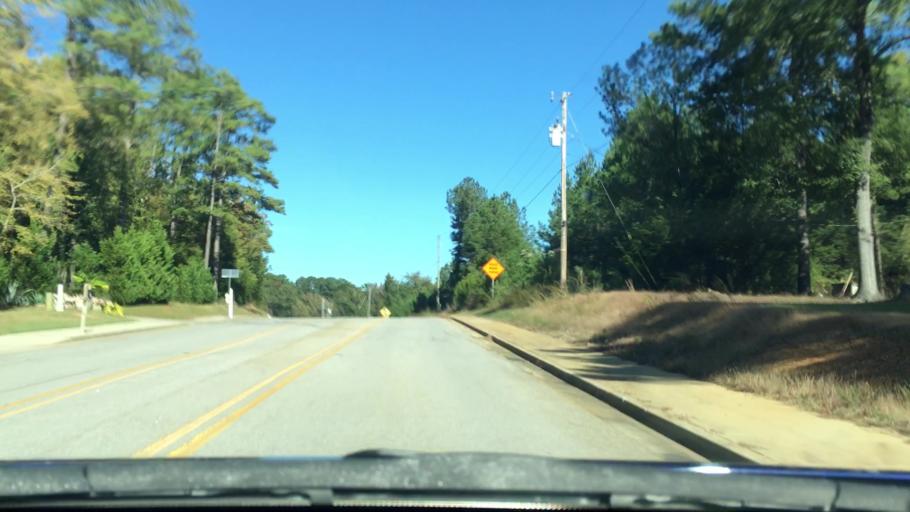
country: US
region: South Carolina
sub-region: Lexington County
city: Irmo
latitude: 34.1125
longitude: -81.1664
